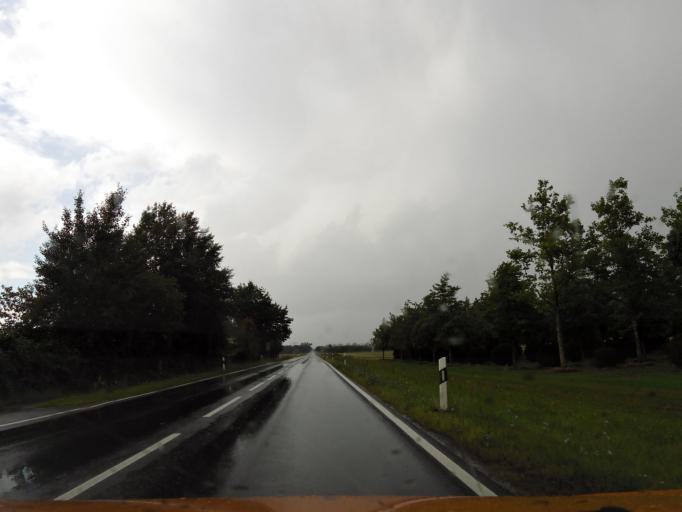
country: DE
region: Brandenburg
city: Wustermark
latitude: 52.4757
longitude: 12.9495
